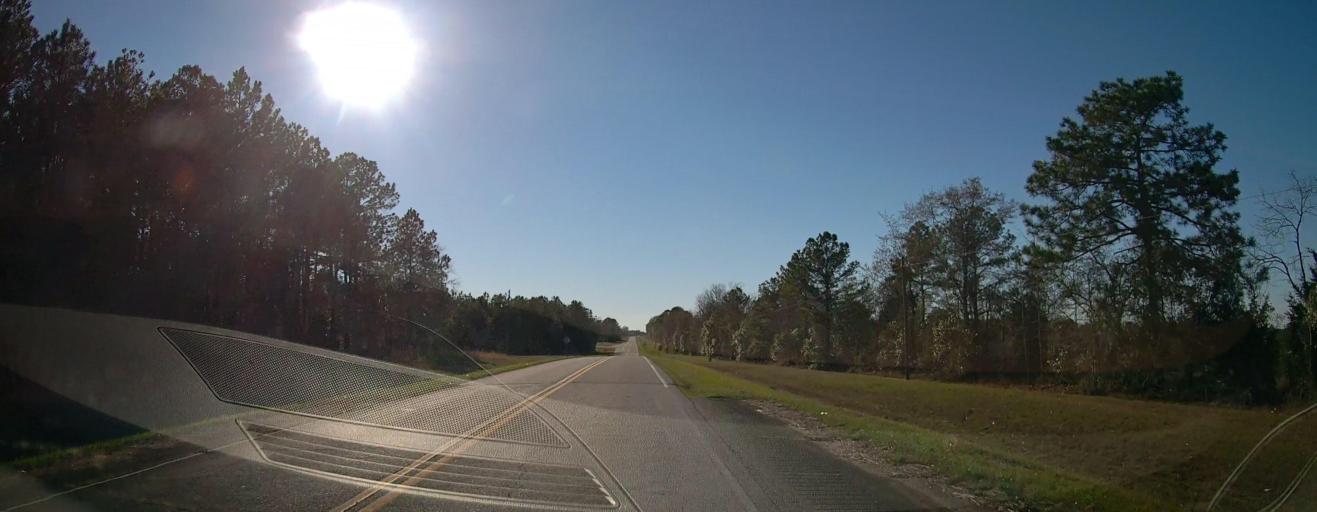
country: US
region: Georgia
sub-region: Taylor County
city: Butler
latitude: 32.5552
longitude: -84.2072
